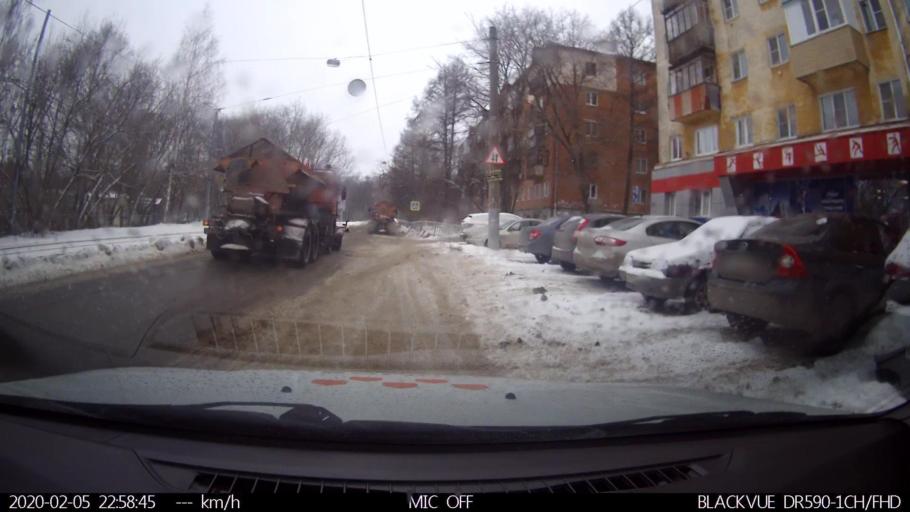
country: RU
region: Penza
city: Bogoslovka
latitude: 53.2244
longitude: 44.8576
